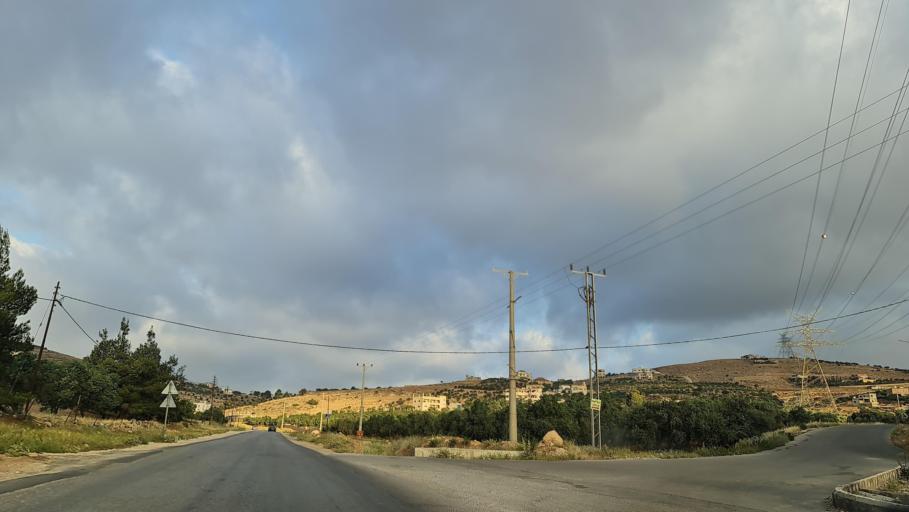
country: JO
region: Amman
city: Al Jubayhah
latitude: 32.0927
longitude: 35.9182
